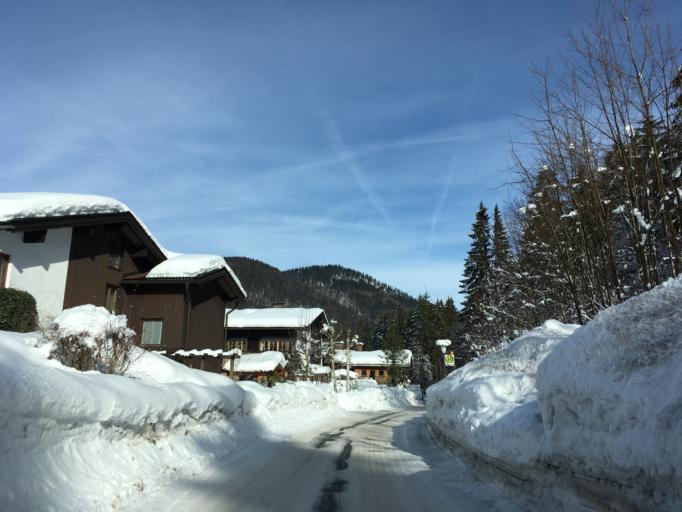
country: DE
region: Bavaria
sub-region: Upper Bavaria
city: Schliersee
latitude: 47.6957
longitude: 11.8923
